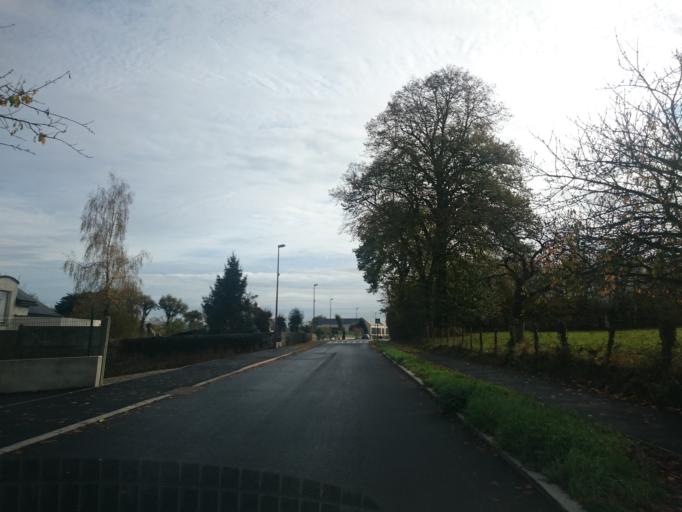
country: FR
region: Brittany
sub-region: Departement d'Ille-et-Vilaine
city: Bourg-des-Comptes
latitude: 47.9284
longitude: -1.7356
